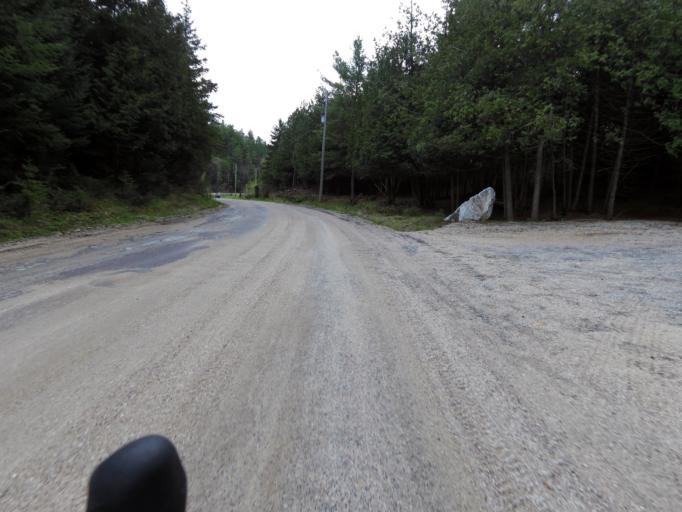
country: CA
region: Quebec
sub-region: Outaouais
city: Wakefield
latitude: 45.6209
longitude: -75.8812
